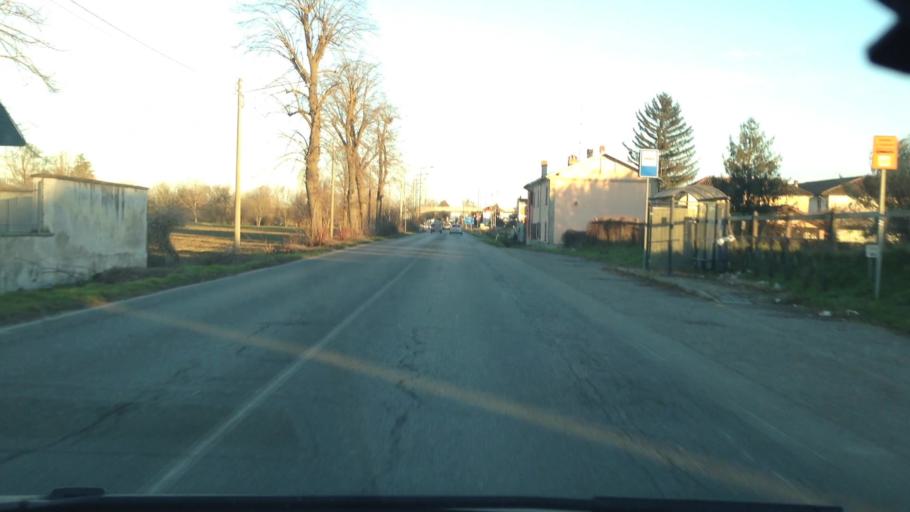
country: IT
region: Piedmont
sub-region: Provincia di Alessandria
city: Alessandria
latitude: 44.9217
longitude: 8.5697
